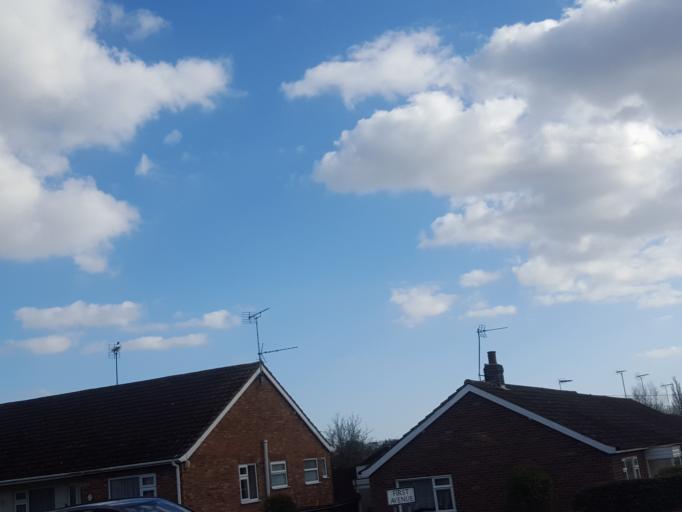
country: GB
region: England
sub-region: Essex
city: Little Clacton
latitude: 51.8559
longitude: 1.1162
